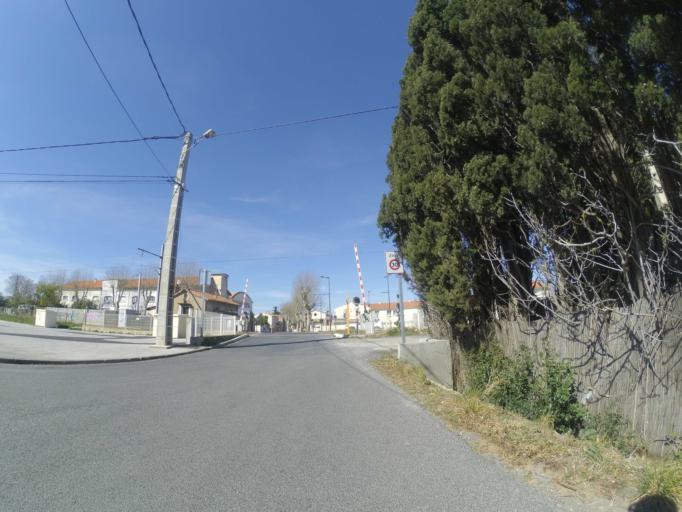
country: FR
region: Languedoc-Roussillon
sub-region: Departement des Pyrenees-Orientales
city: Le Soler
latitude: 42.6789
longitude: 2.7967
